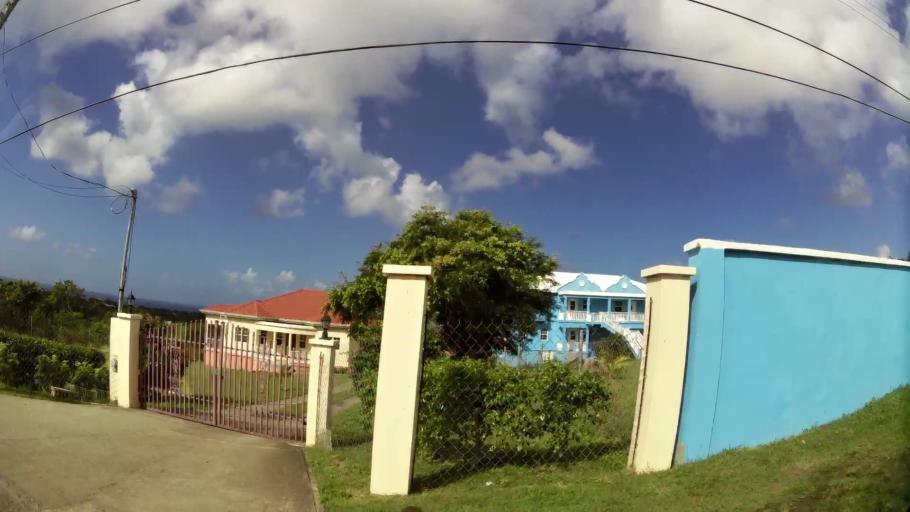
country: KN
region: Saint Paul Charlestown
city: Charlestown
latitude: 17.1331
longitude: -62.6130
